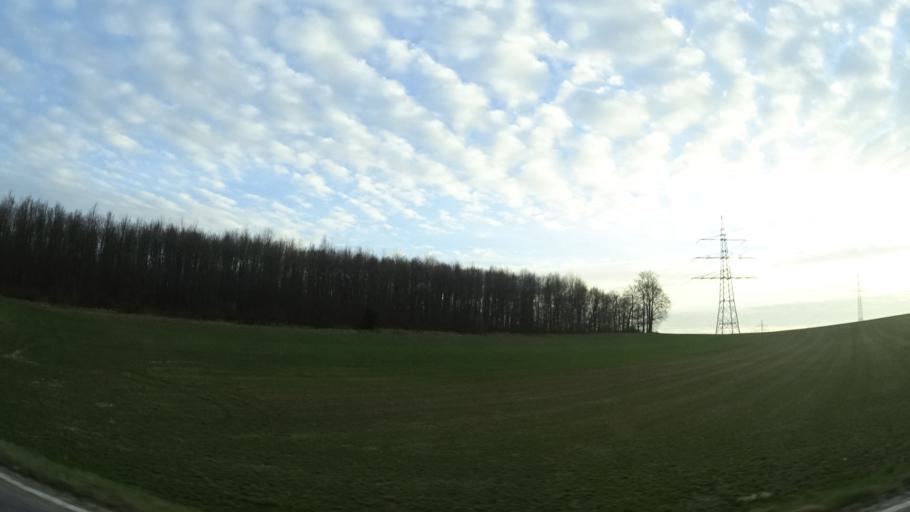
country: DE
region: Baden-Wuerttemberg
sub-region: Regierungsbezirk Stuttgart
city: Hemmingen
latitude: 48.8811
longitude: 9.0115
